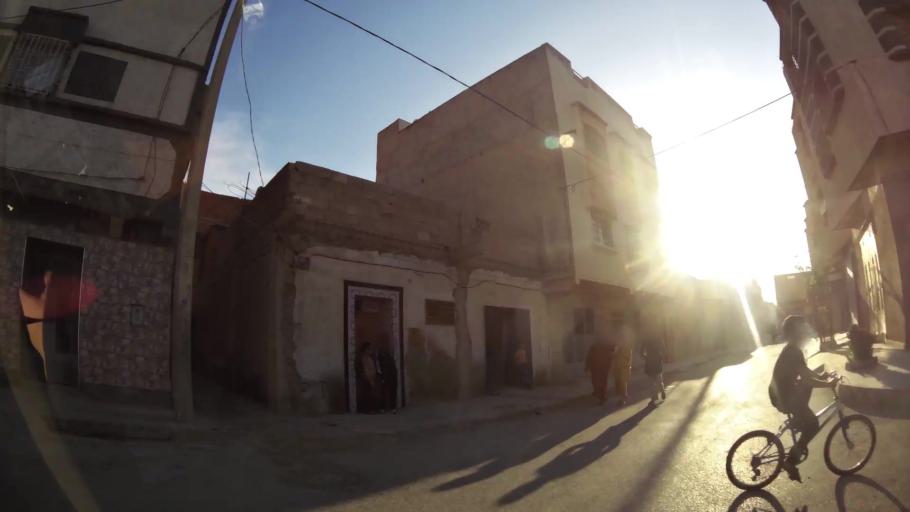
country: MA
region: Oriental
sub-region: Oujda-Angad
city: Oujda
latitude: 34.7024
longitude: -1.9061
